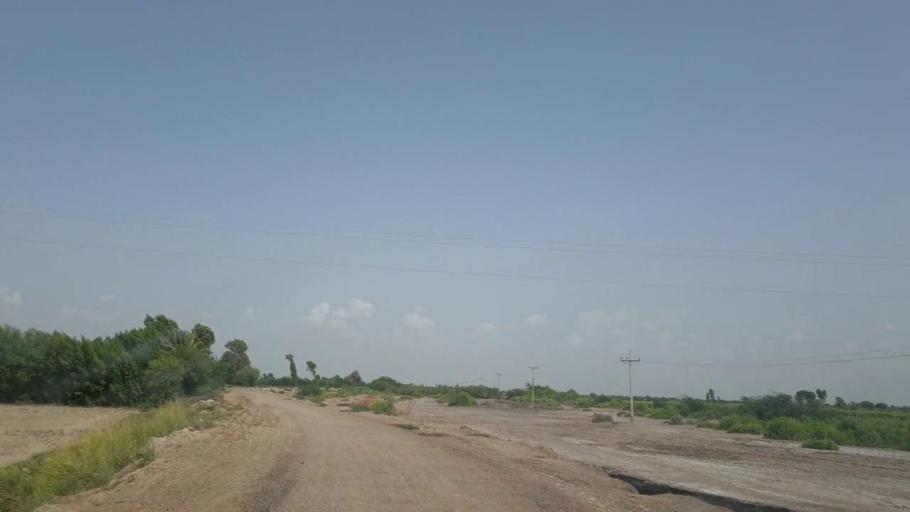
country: PK
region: Sindh
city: Tando Bago
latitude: 24.7586
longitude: 69.1746
